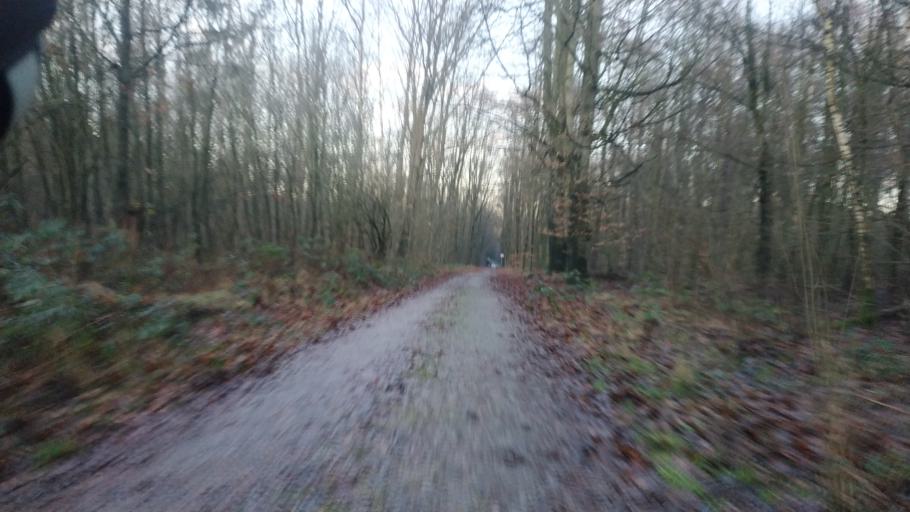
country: DE
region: North Rhine-Westphalia
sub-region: Regierungsbezirk Munster
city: Mettingen
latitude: 52.2861
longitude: 7.7825
